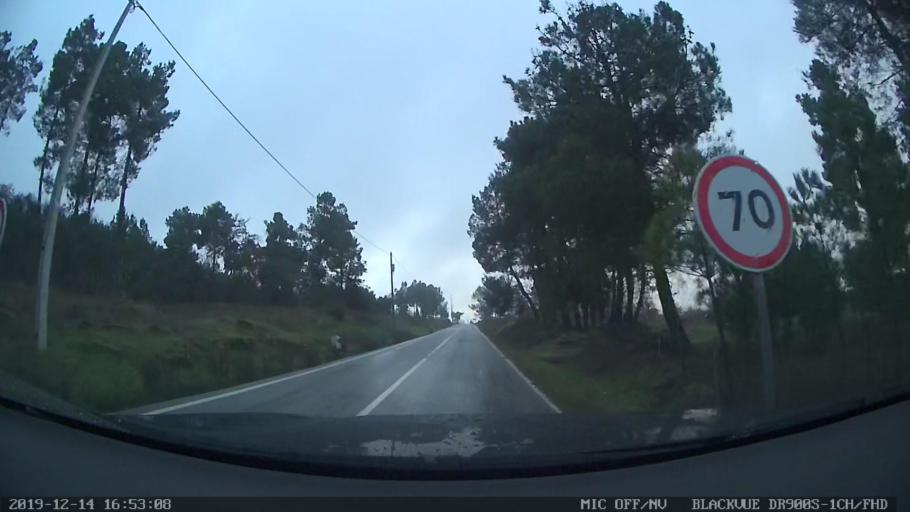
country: PT
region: Vila Real
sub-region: Murca
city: Murca
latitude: 41.4279
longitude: -7.5161
